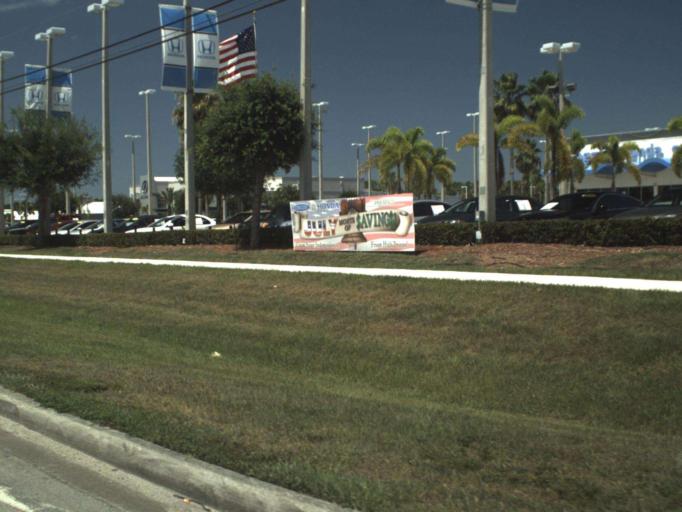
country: US
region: Florida
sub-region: Saint Lucie County
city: White City
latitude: 27.3816
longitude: -80.3258
